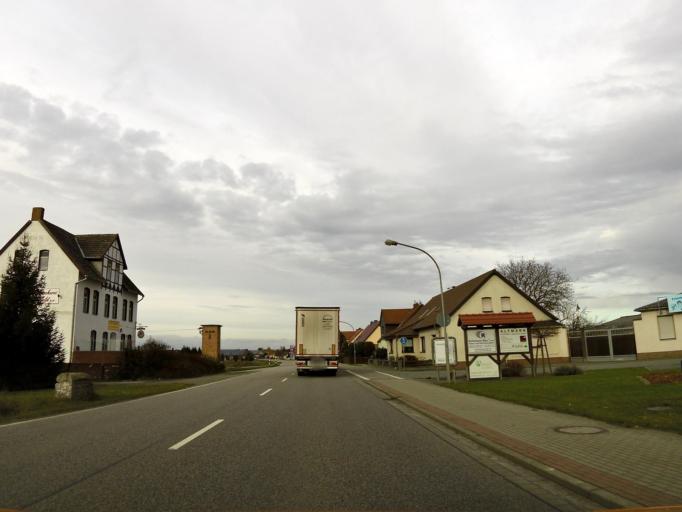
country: DE
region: Saxony-Anhalt
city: Pretzier
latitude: 52.7347
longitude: 11.2449
